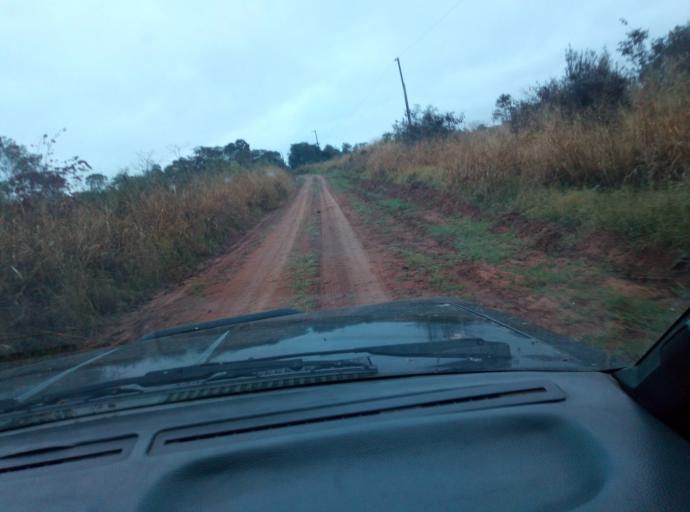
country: PY
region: Caaguazu
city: Carayao
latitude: -25.1904
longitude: -56.3511
